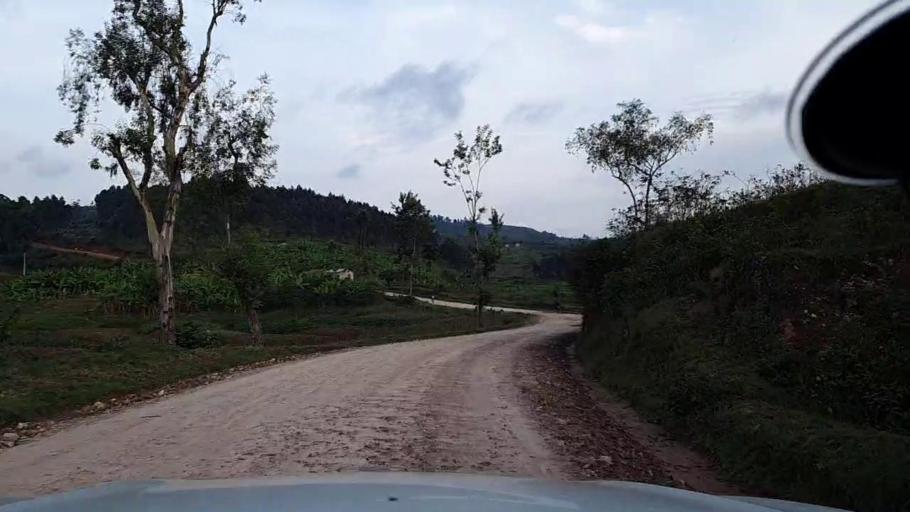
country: RW
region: Southern Province
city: Nyanza
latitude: -2.2145
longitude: 29.6247
